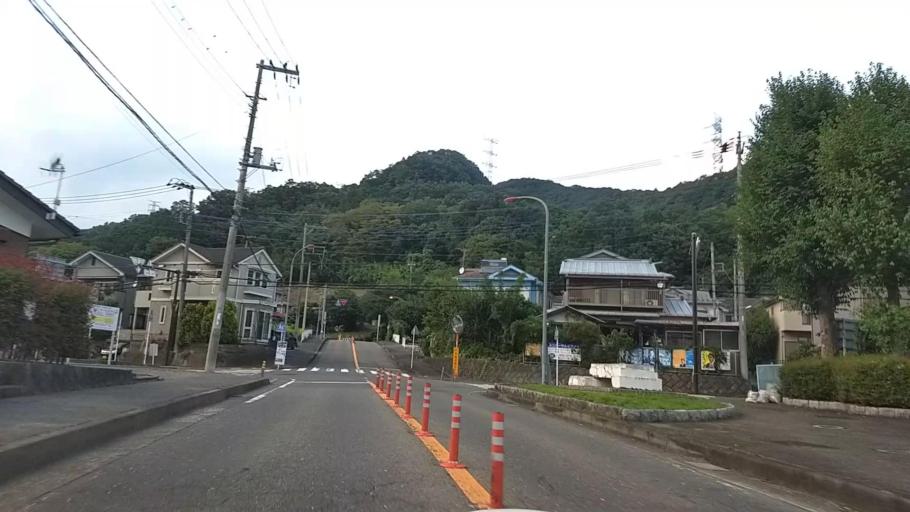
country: JP
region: Yamanashi
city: Uenohara
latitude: 35.6122
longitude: 139.2163
